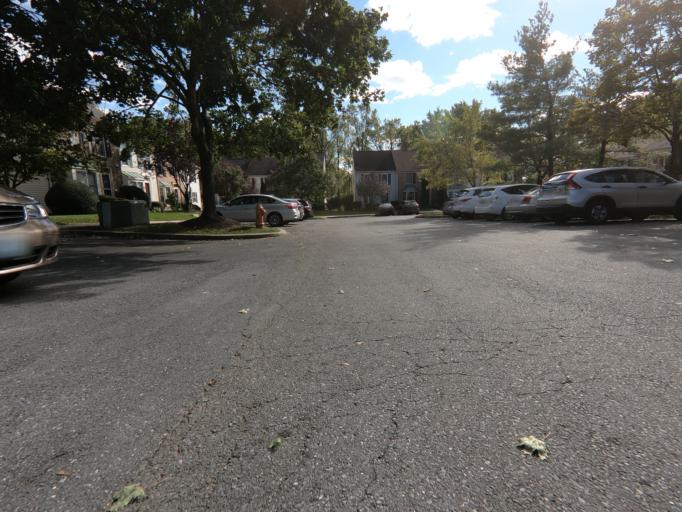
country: US
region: Maryland
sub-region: Howard County
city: Ellicott City
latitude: 39.2655
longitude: -76.8176
